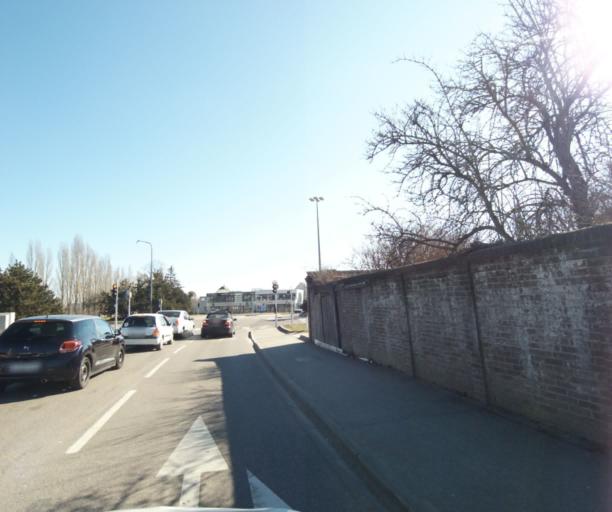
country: FR
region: Lorraine
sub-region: Departement de Meurthe-et-Moselle
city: Tomblaine
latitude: 48.6936
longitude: 6.2112
